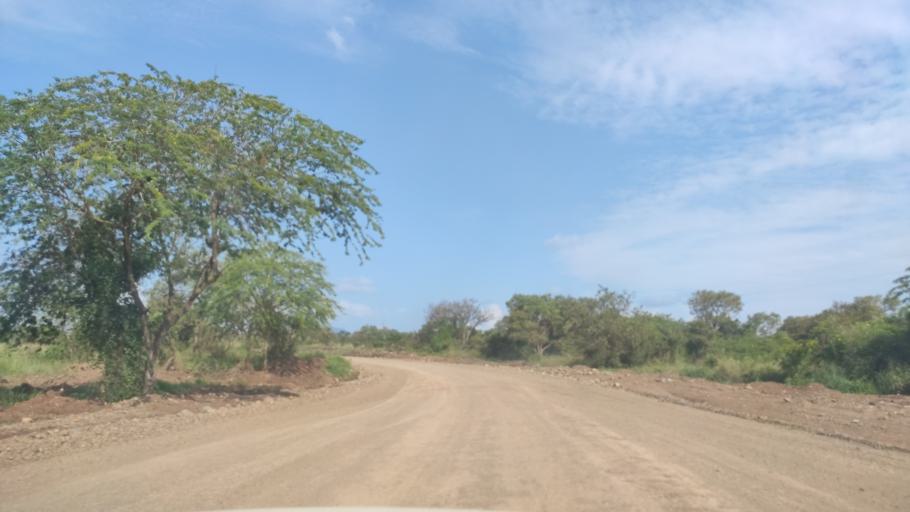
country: ET
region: Southern Nations, Nationalities, and People's Region
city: Felege Neway
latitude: 6.4280
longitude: 37.2076
